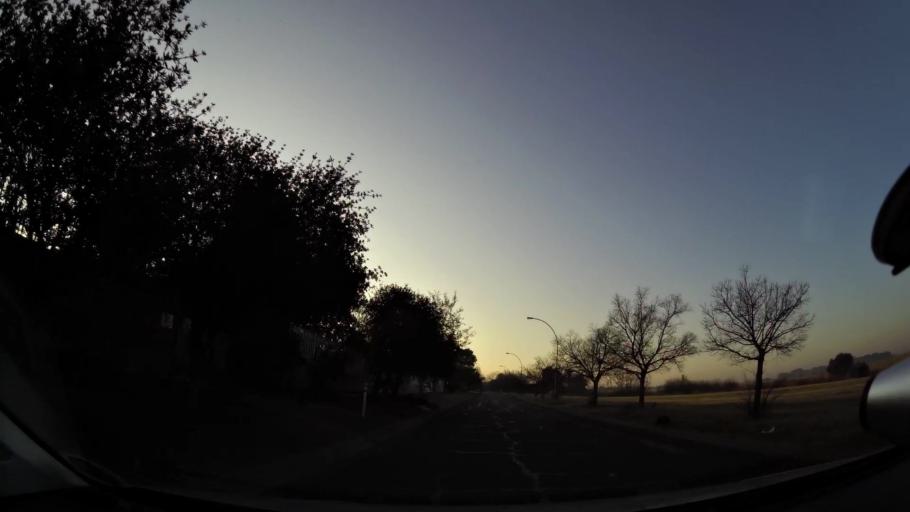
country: ZA
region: Orange Free State
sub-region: Mangaung Metropolitan Municipality
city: Bloemfontein
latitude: -29.1069
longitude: 26.1501
